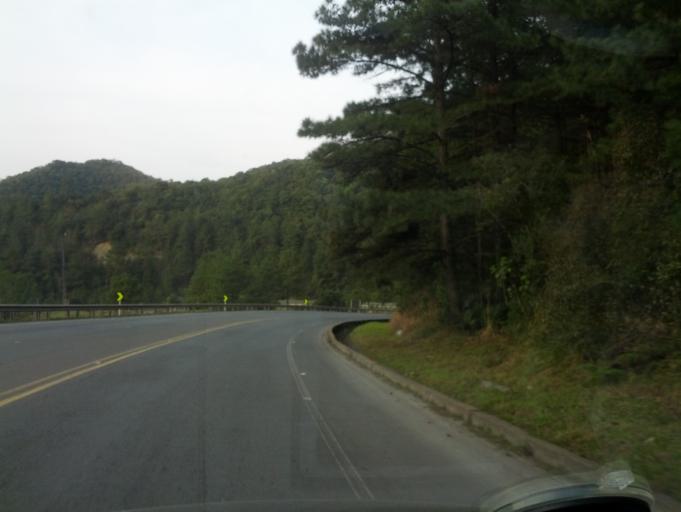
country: BR
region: Santa Catarina
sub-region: Otacilio Costa
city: Otacilio Costa
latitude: -27.3024
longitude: -50.0778
